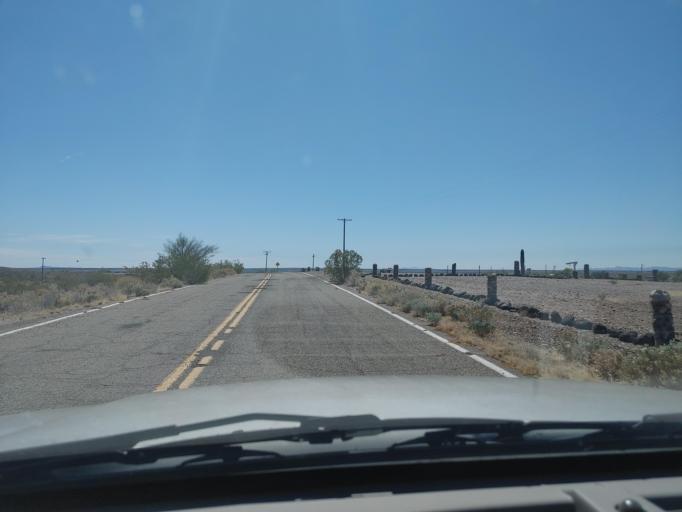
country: US
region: Arizona
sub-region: Maricopa County
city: Gila Bend
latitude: 32.9906
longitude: -113.3356
